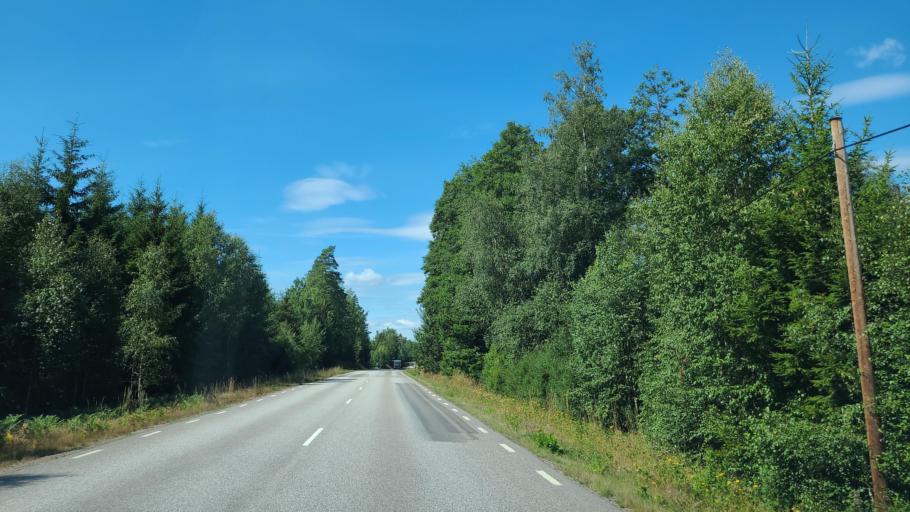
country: SE
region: Kalmar
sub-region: Nybro Kommun
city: Nybro
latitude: 56.5621
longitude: 15.7737
